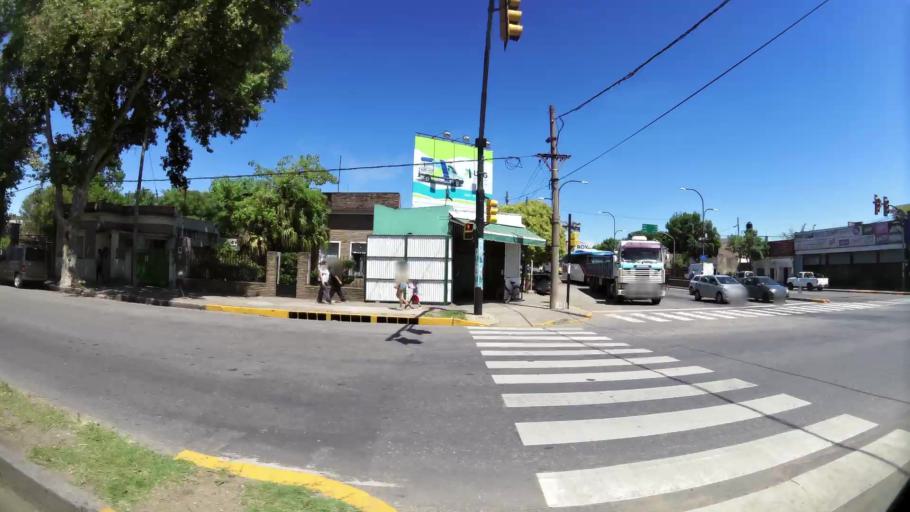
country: AR
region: Santa Fe
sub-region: Departamento de Rosario
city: Rosario
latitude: -32.9487
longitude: -60.7124
